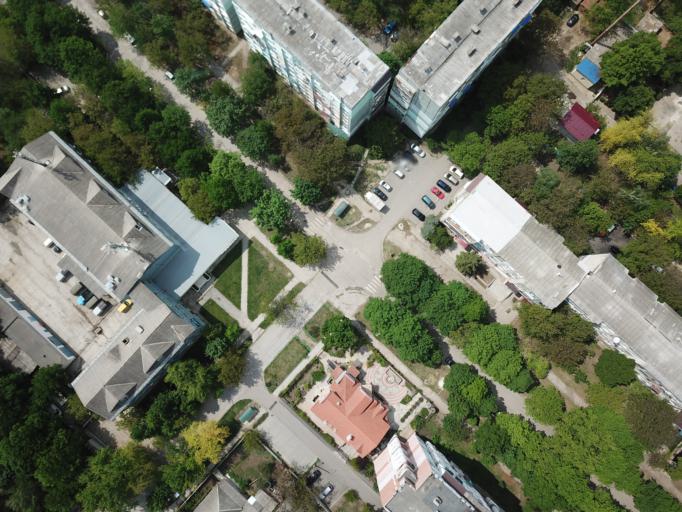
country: MD
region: Ungheni
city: Ungheni
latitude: 47.2149
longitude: 27.7986
